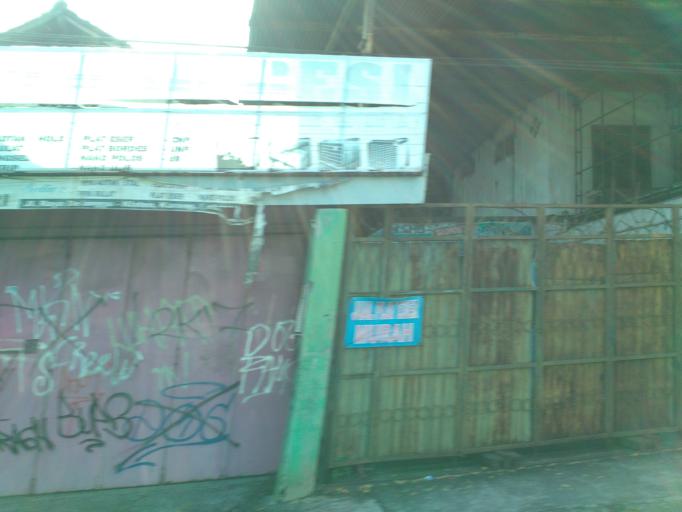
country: ID
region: Central Java
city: Delanggu
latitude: -7.6298
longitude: 110.6946
